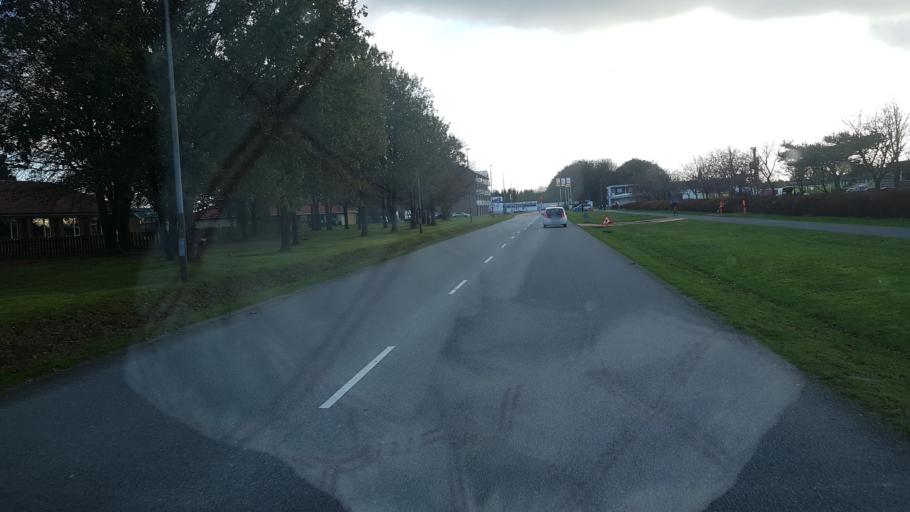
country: DK
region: South Denmark
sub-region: Billund Kommune
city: Grindsted
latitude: 55.7628
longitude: 8.9156
